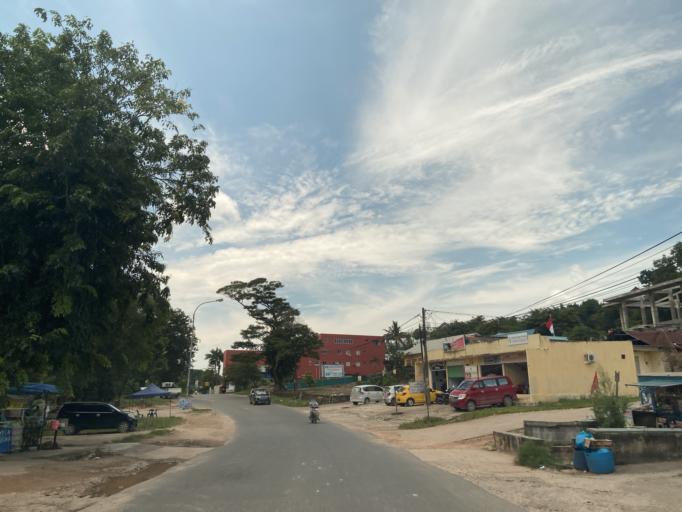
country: SG
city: Singapore
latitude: 1.1588
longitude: 104.0208
